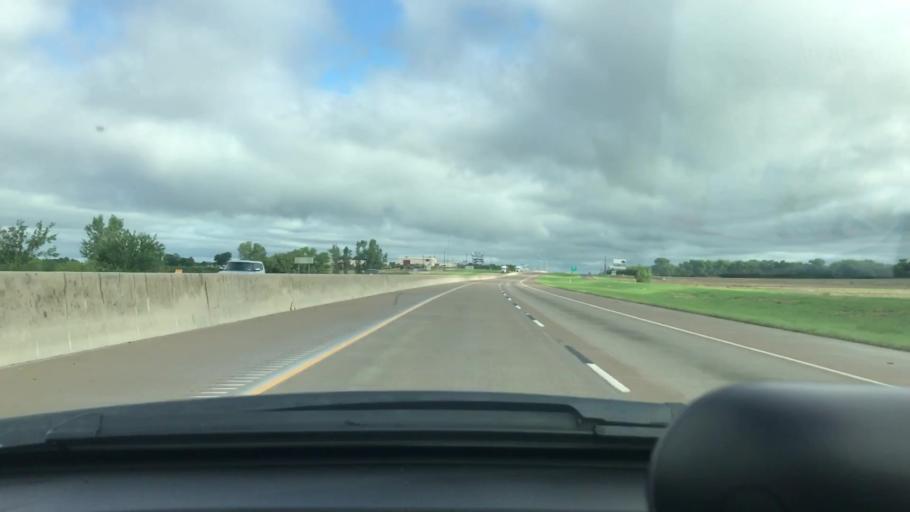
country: US
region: Texas
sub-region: Grayson County
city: Howe
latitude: 33.4812
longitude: -96.6196
